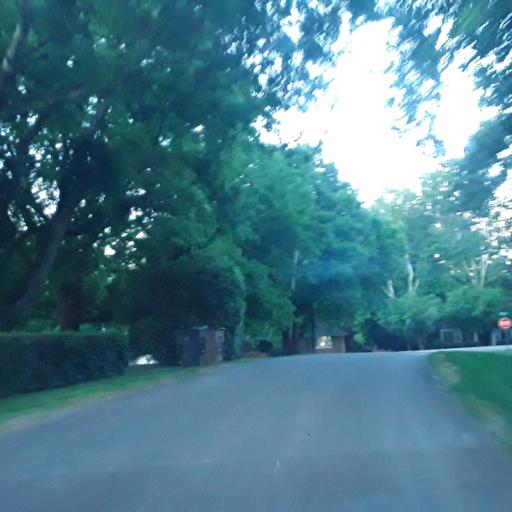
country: US
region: Tennessee
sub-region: Davidson County
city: Oak Hill
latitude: 36.0676
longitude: -86.7656
